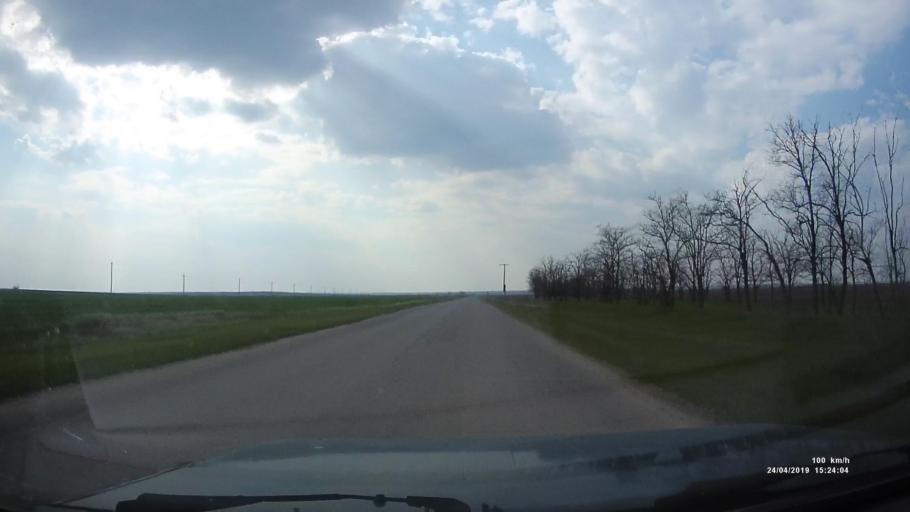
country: RU
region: Rostov
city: Remontnoye
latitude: 46.5463
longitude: 43.0765
